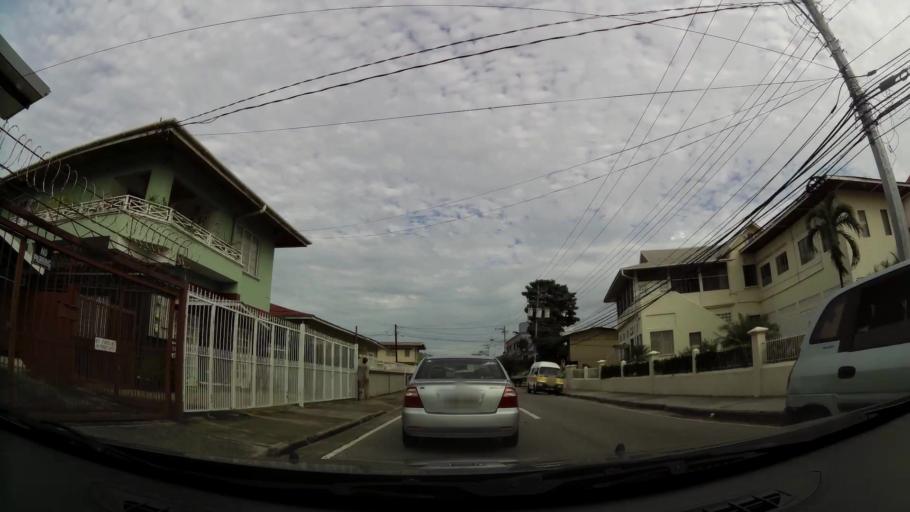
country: TT
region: City of Port of Spain
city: Port-of-Spain
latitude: 10.6659
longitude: -61.5274
